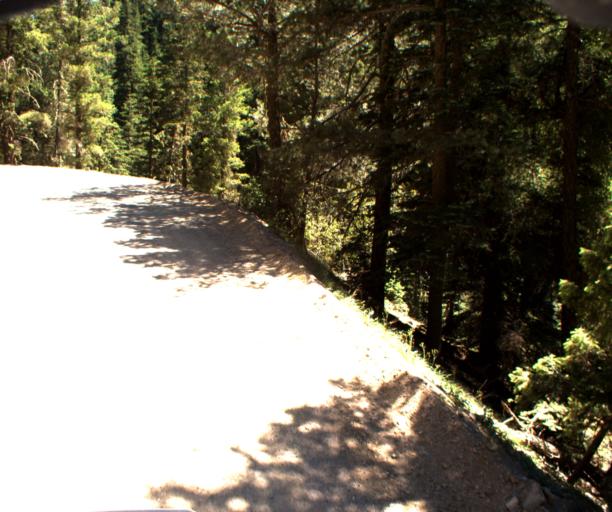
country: US
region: Arizona
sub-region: Graham County
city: Swift Trail Junction
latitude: 32.6731
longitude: -109.8871
